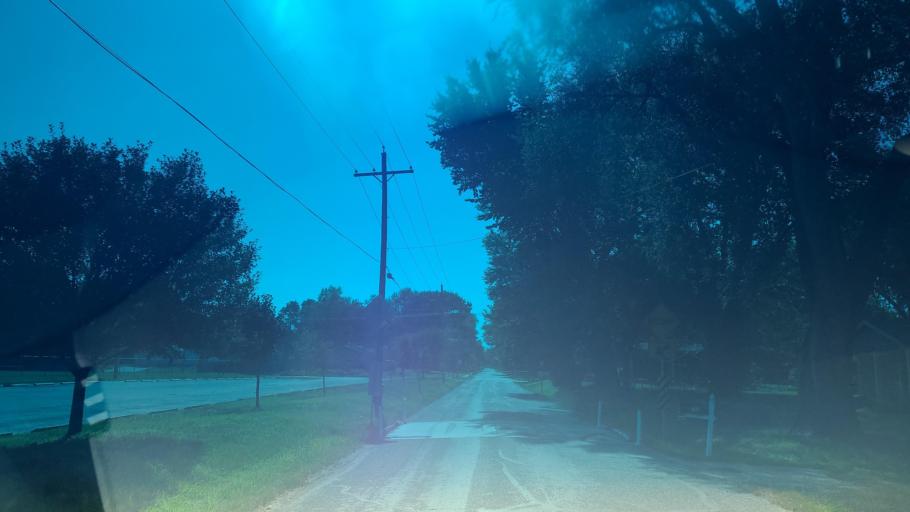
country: US
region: Kansas
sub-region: Douglas County
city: Lawrence
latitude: 38.9824
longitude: -95.2226
